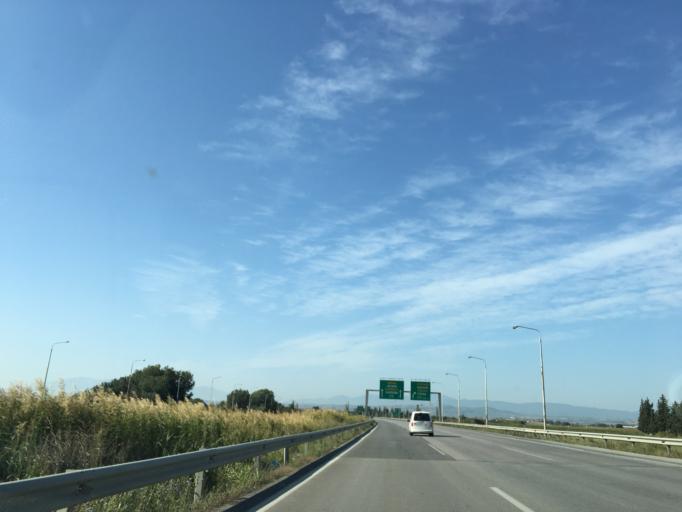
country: GR
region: Central Macedonia
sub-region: Nomos Imathias
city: Kleidi
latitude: 40.5632
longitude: 22.6067
